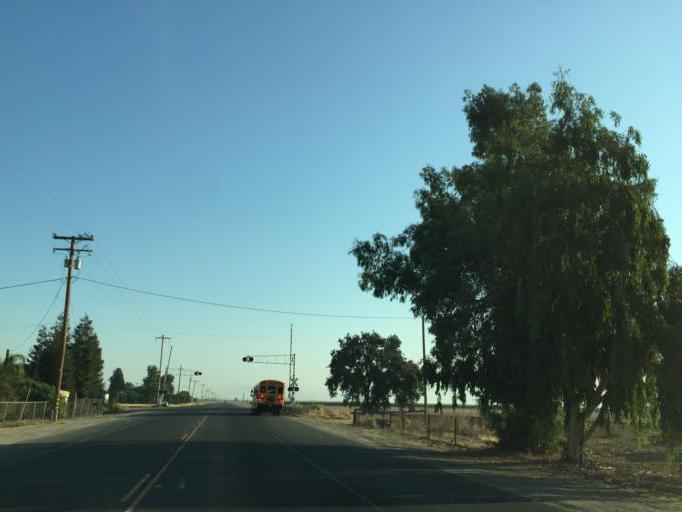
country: US
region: California
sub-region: Tulare County
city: Cutler
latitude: 36.4542
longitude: -119.2955
